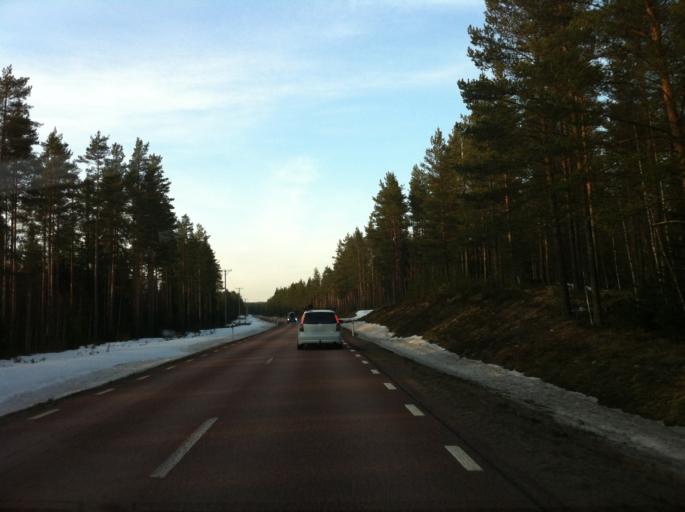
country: SE
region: Vaermland
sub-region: Filipstads Kommun
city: Lesjofors
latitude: 60.1630
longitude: 14.2045
